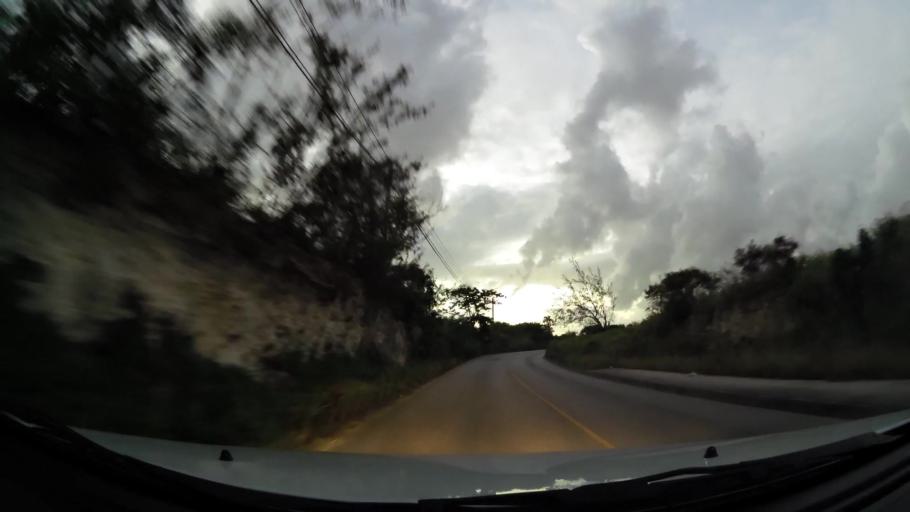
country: BB
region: Saint Philip
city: Crane
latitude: 13.1183
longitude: -59.4933
